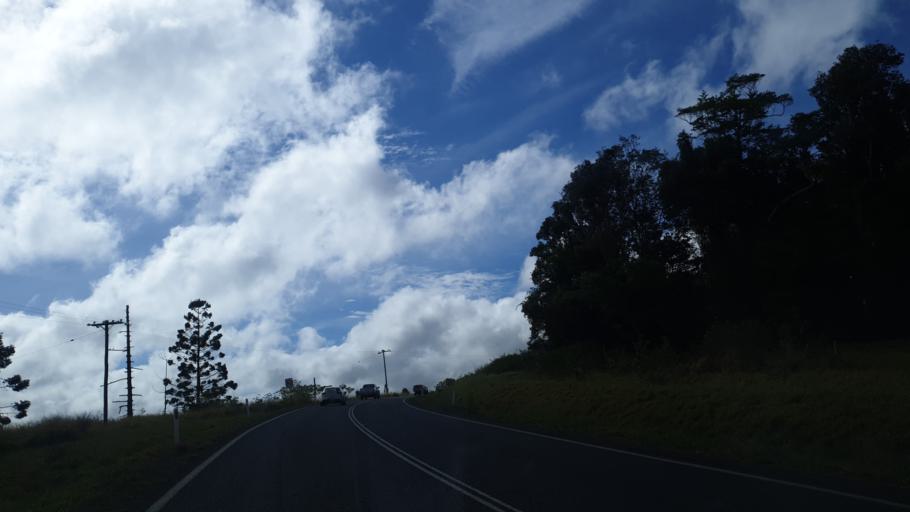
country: AU
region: Queensland
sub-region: Tablelands
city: Atherton
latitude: -17.3464
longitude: 145.5788
